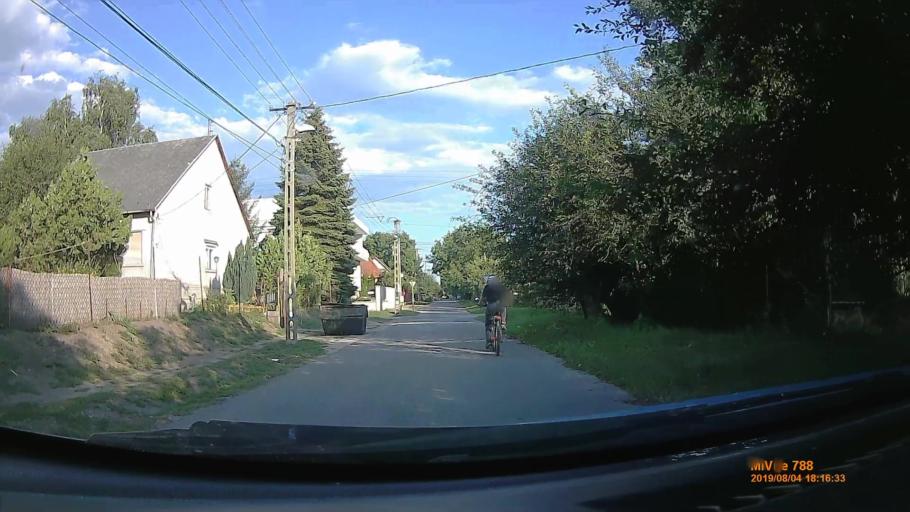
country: HU
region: Pest
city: God
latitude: 47.7020
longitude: 19.1529
